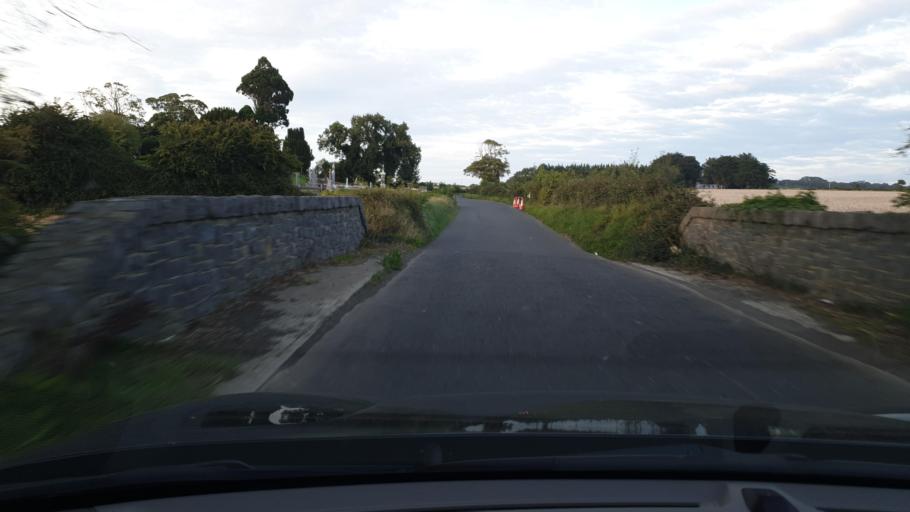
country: IE
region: Leinster
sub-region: An Mhi
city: Ashbourne
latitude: 53.5456
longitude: -6.3303
